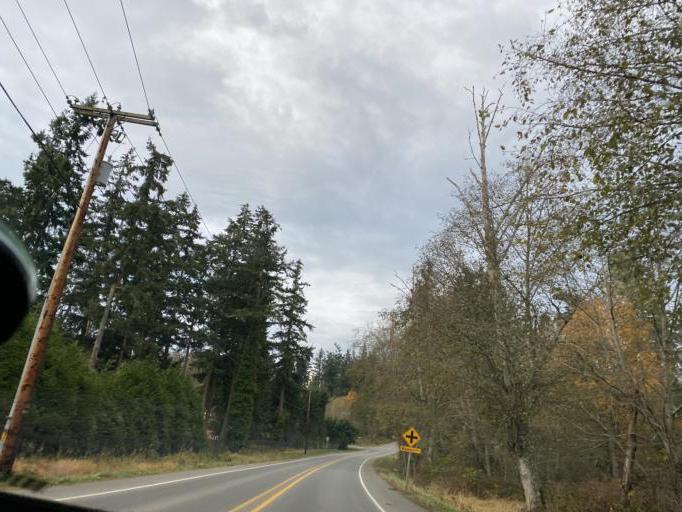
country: US
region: Washington
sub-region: Island County
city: Freeland
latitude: 48.0012
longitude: -122.5345
